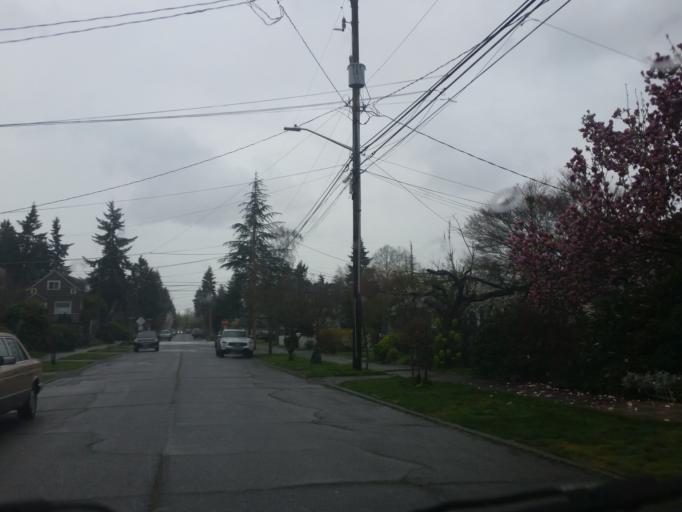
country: US
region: Washington
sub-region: King County
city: Shoreline
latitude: 47.6896
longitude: -122.3392
